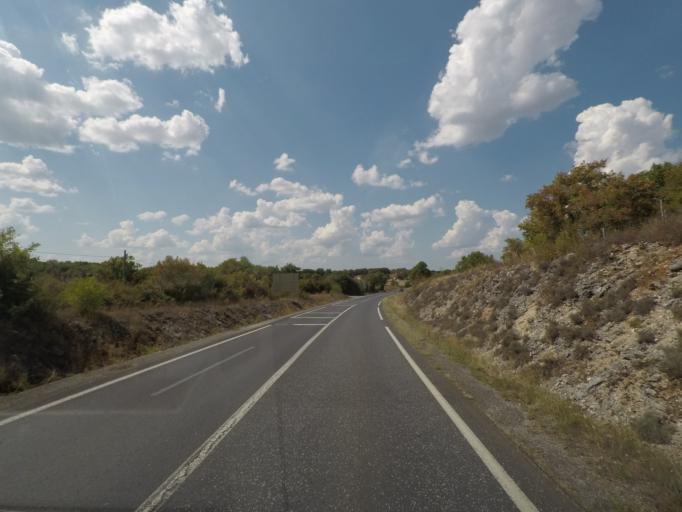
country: FR
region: Midi-Pyrenees
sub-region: Departement du Lot
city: Gramat
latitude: 44.6860
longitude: 1.6039
